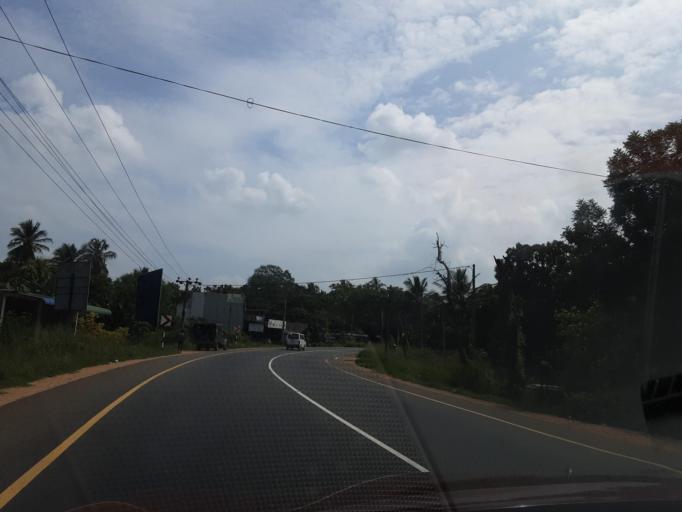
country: LK
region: North Central
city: Anuradhapura
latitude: 8.5024
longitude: 80.5115
